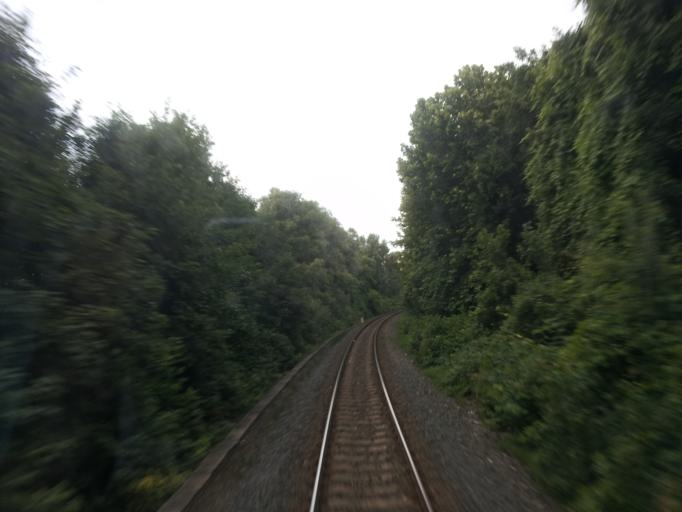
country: HU
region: Veszprem
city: Balatonalmadi
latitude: 47.0460
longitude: 18.0271
